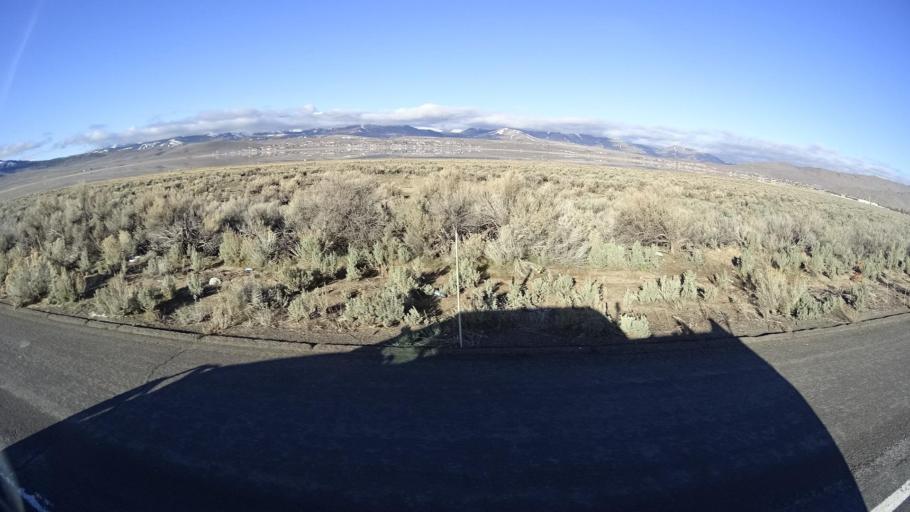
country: US
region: Nevada
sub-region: Washoe County
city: Cold Springs
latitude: 39.6629
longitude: -119.9606
